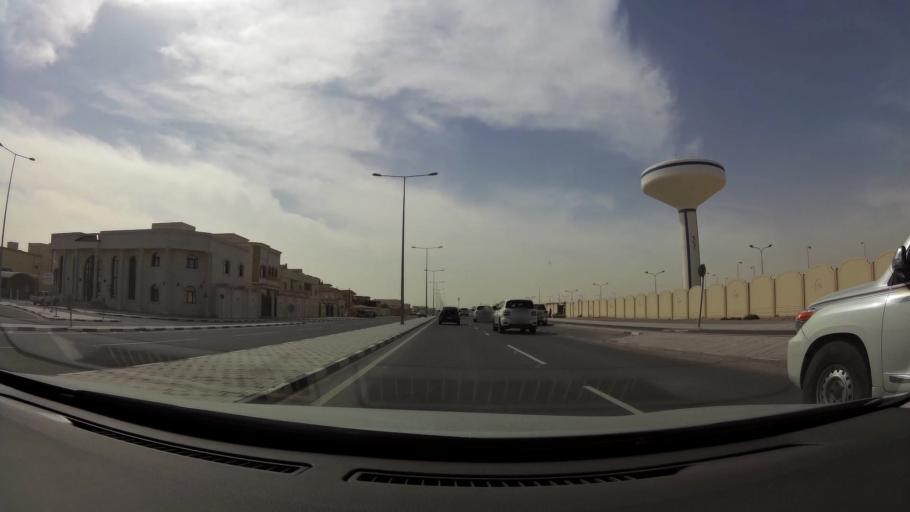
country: QA
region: Baladiyat ar Rayyan
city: Ar Rayyan
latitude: 25.3198
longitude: 51.4045
